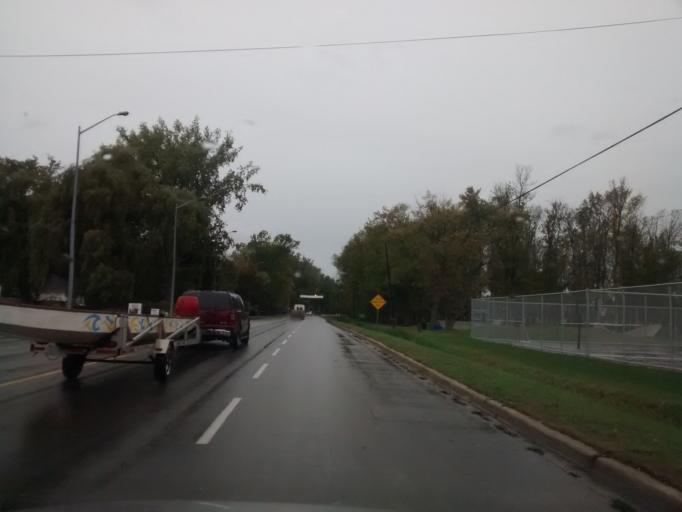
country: CA
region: Ontario
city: Welland
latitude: 42.9063
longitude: -79.6320
